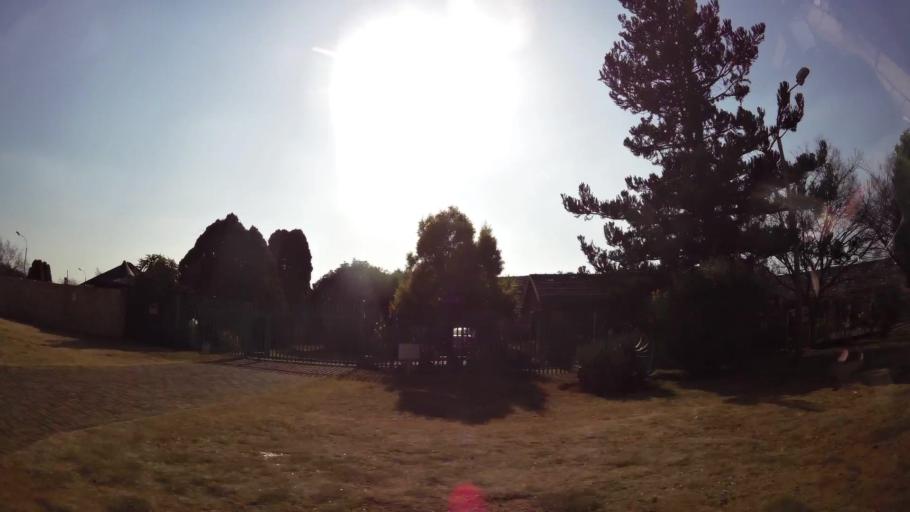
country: ZA
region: Gauteng
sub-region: West Rand District Municipality
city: Randfontein
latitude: -26.1804
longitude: 27.6880
